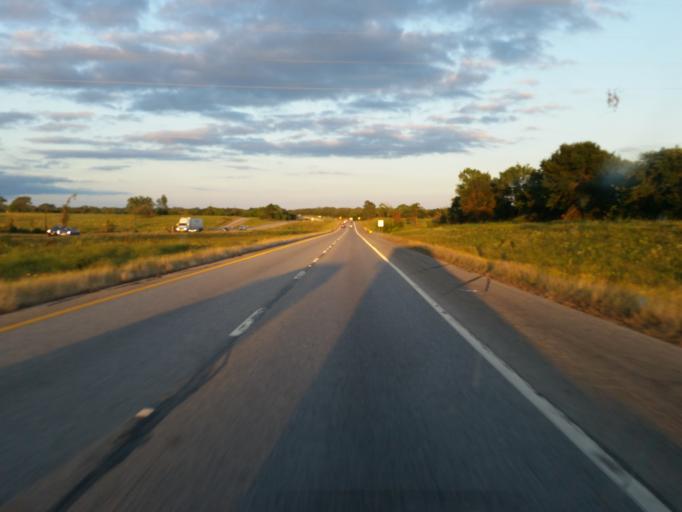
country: US
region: Texas
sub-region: Van Zandt County
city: Van
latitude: 32.5046
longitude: -95.6348
